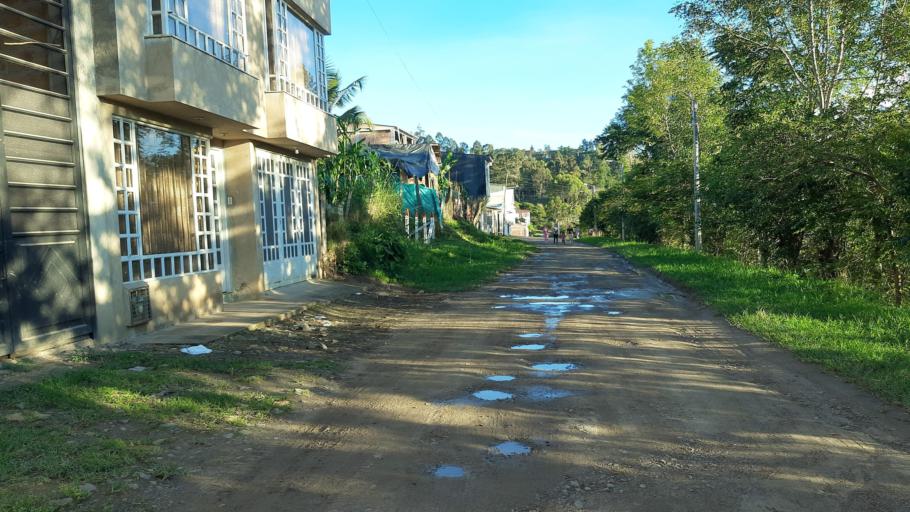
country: CO
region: Boyaca
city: Garagoa
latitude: 5.0832
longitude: -73.3682
